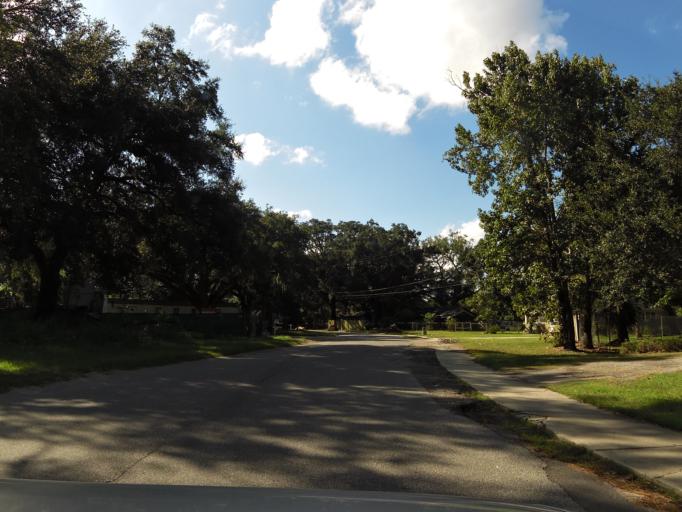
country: US
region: Florida
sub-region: Duval County
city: Jacksonville
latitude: 30.2767
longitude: -81.6394
